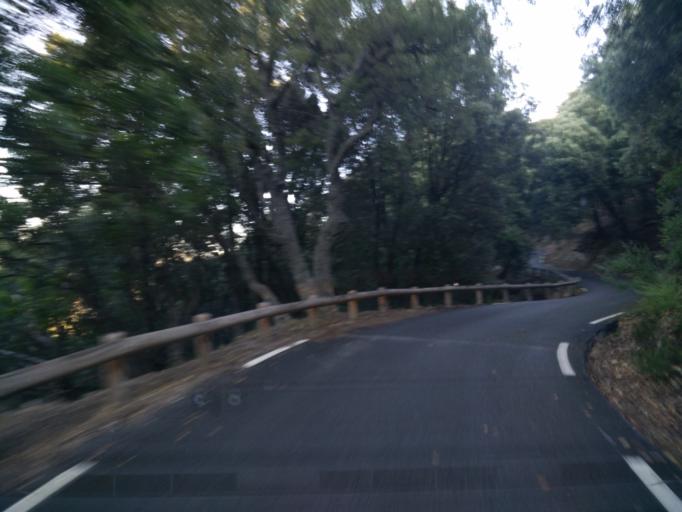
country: FR
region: Provence-Alpes-Cote d'Azur
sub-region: Departement du Var
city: Collobrieres
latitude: 43.2357
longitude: 6.3788
